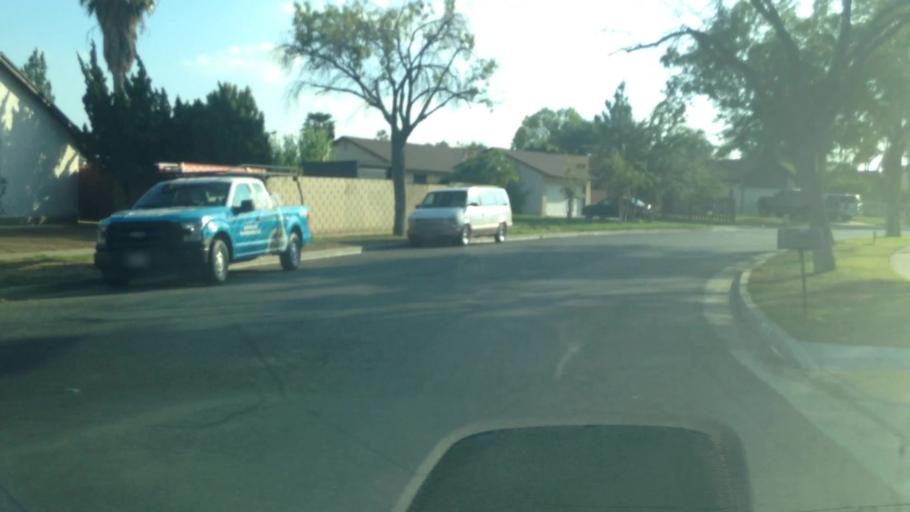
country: US
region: California
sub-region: Riverside County
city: Pedley
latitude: 33.9538
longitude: -117.4692
